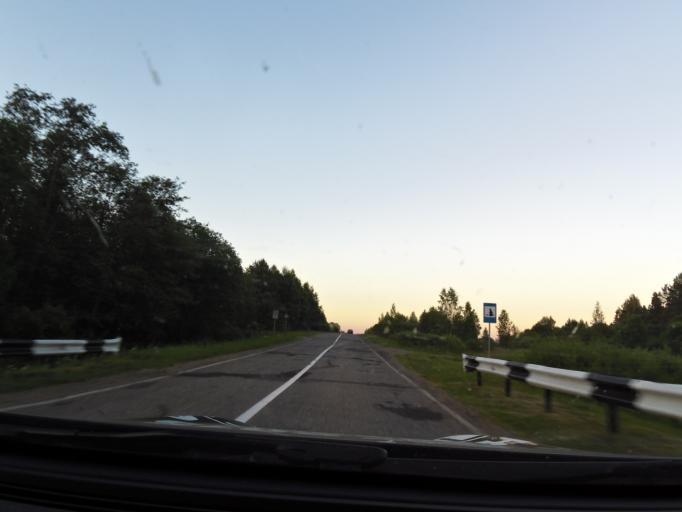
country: RU
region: Jaroslavl
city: Lyubim
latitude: 58.3408
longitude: 40.8474
